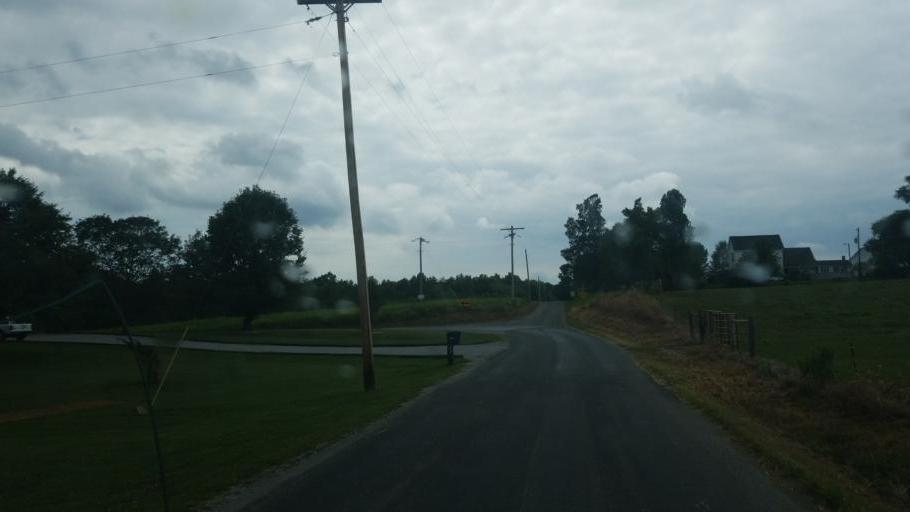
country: US
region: Illinois
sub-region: Jackson County
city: Murphysboro
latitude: 37.7019
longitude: -89.3377
